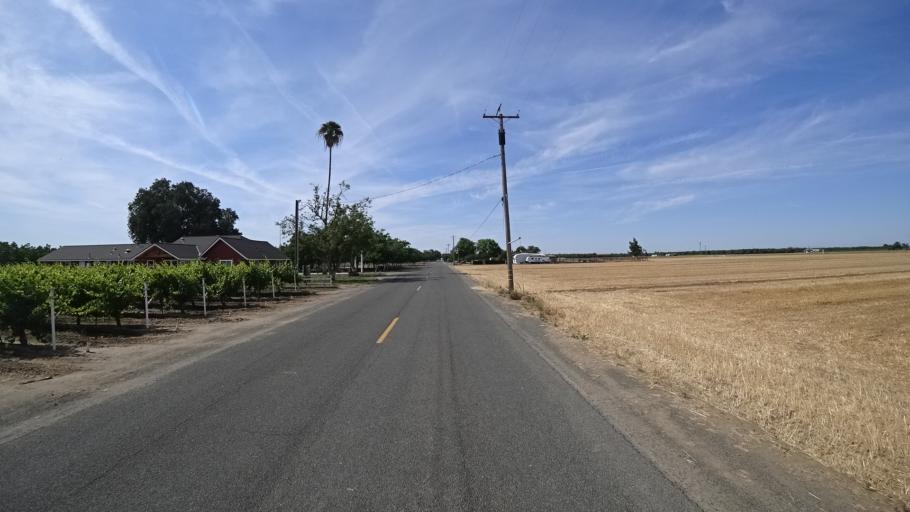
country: US
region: California
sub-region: Kings County
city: Lucerne
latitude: 36.3849
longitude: -119.6100
